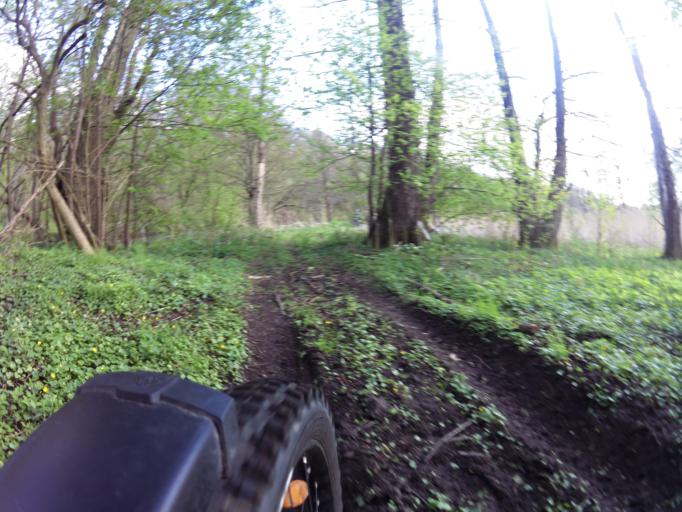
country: PL
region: West Pomeranian Voivodeship
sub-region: Powiat gryficki
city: Ploty
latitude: 53.7894
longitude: 15.2622
